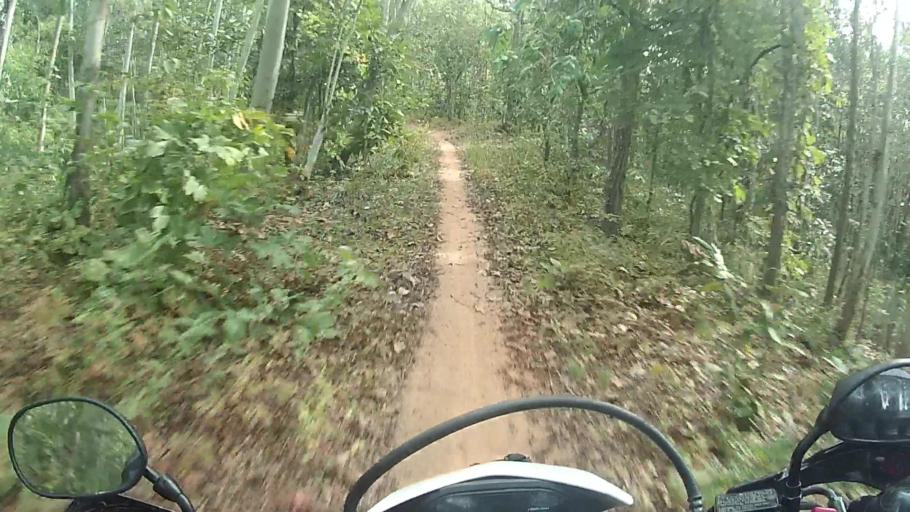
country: TH
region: Chiang Mai
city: Mae On
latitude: 18.7269
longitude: 99.2911
